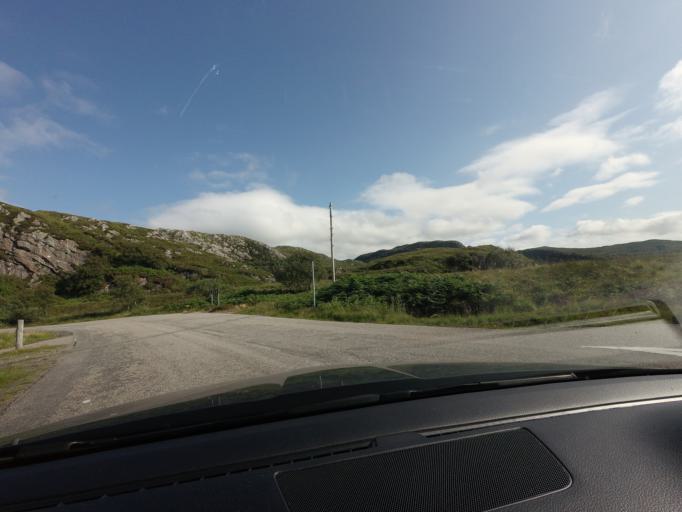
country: GB
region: Scotland
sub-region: Highland
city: Ullapool
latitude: 58.3738
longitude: -5.0169
